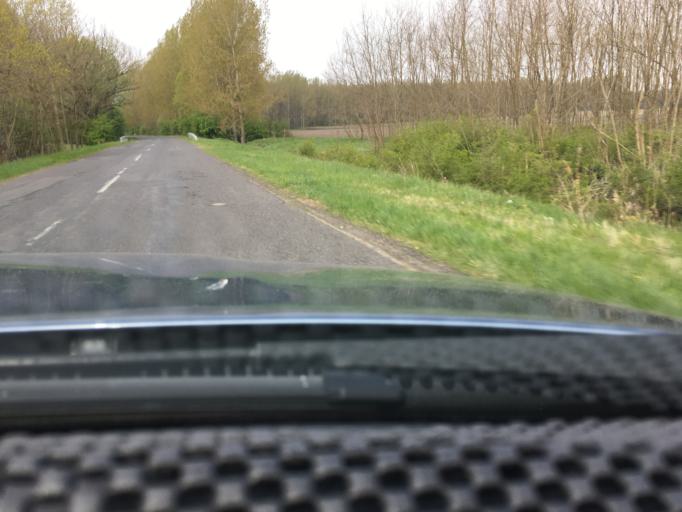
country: HU
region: Szabolcs-Szatmar-Bereg
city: Nyirlugos
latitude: 47.6949
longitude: 22.0811
